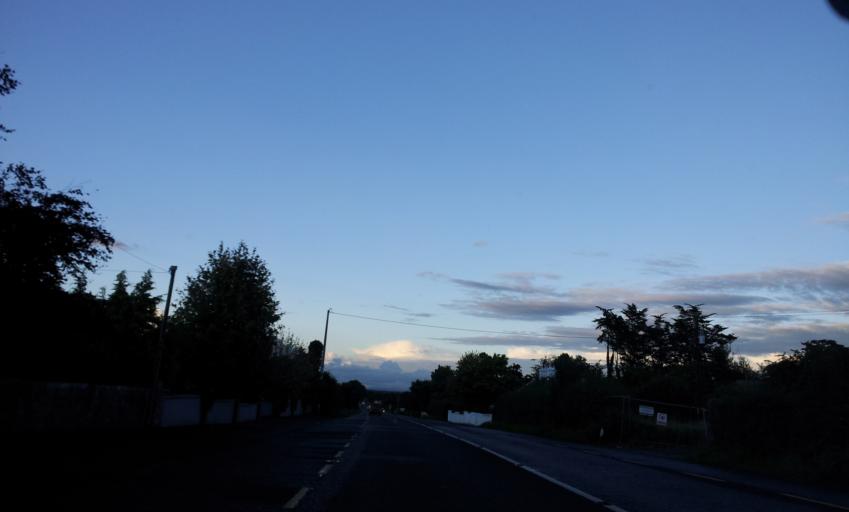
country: IE
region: Munster
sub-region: County Limerick
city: Newcastle West
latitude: 52.4582
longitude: -9.0334
